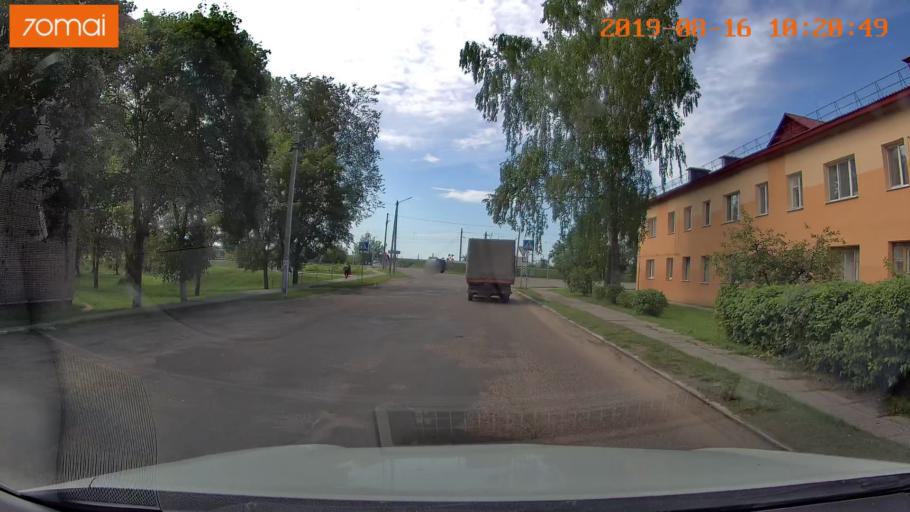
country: BY
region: Mogilev
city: Asipovichy
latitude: 53.2978
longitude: 28.6605
